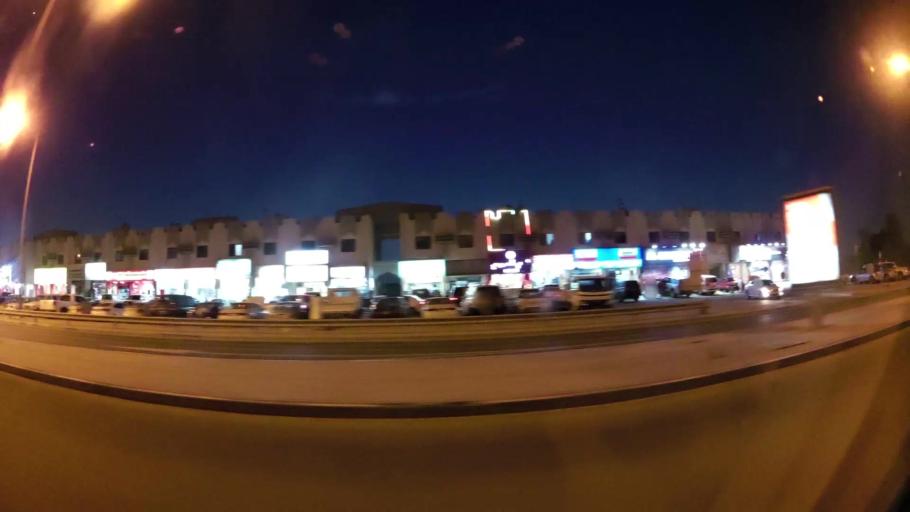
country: QA
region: Baladiyat ar Rayyan
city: Ar Rayyan
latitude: 25.2874
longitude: 51.4311
